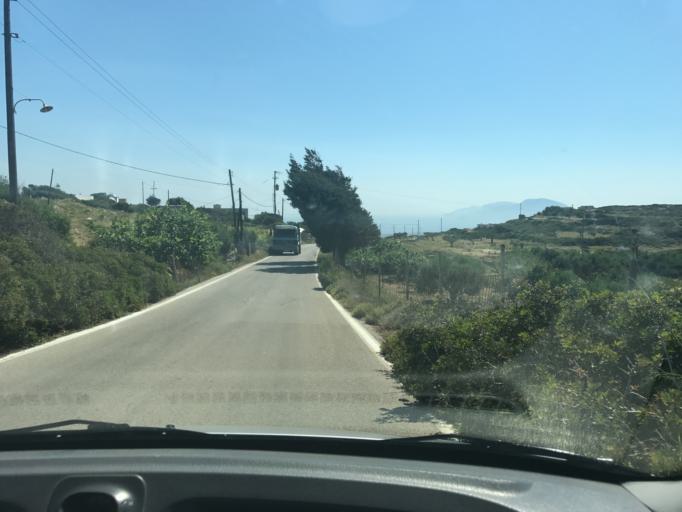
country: GR
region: South Aegean
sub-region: Nomos Dodekanisou
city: Karpathos
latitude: 35.4795
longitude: 27.1529
